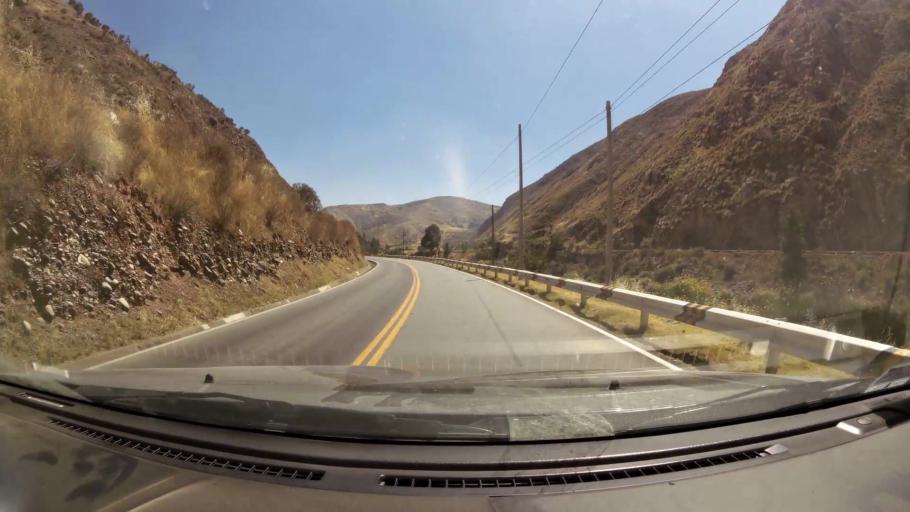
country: PE
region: Junin
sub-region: Provincia de Jauja
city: Parco
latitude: -11.7870
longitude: -75.5523
